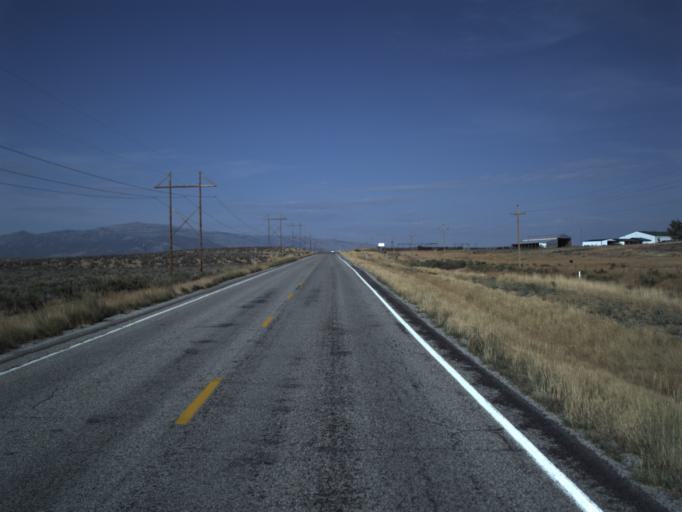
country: US
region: Idaho
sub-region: Oneida County
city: Malad City
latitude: 41.9659
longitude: -112.9891
